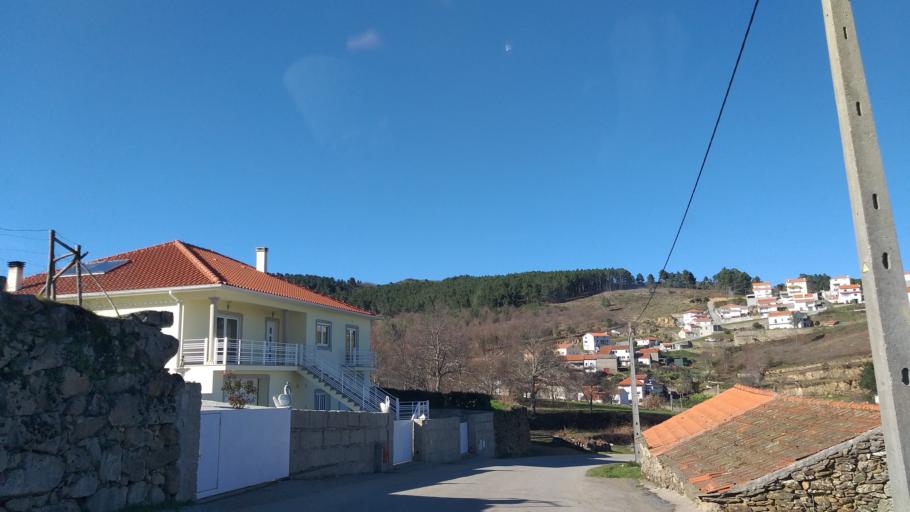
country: PT
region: Guarda
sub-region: Celorico da Beira
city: Celorico da Beira
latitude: 40.5166
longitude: -7.3941
